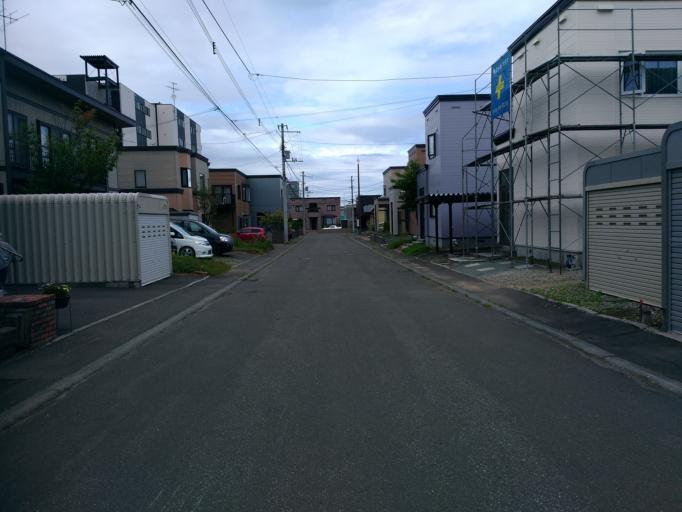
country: JP
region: Hokkaido
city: Ebetsu
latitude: 43.0848
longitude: 141.5201
